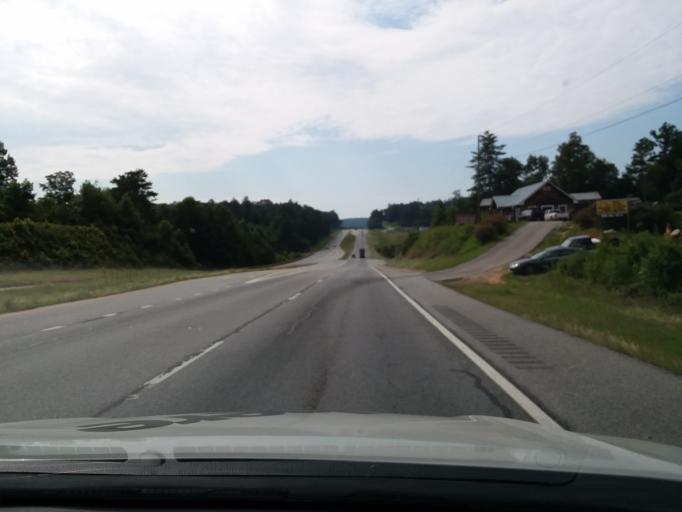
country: US
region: Georgia
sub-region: Rabun County
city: Clayton
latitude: 34.7954
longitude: -83.4153
